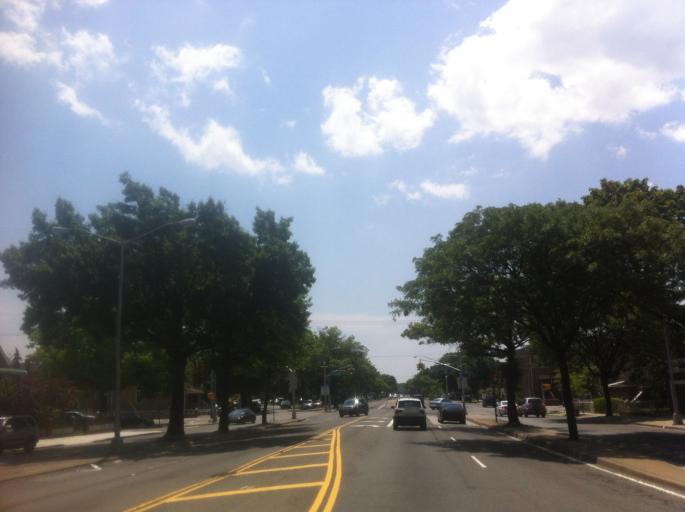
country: US
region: New York
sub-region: Kings County
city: Brooklyn
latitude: 40.6460
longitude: -73.9248
